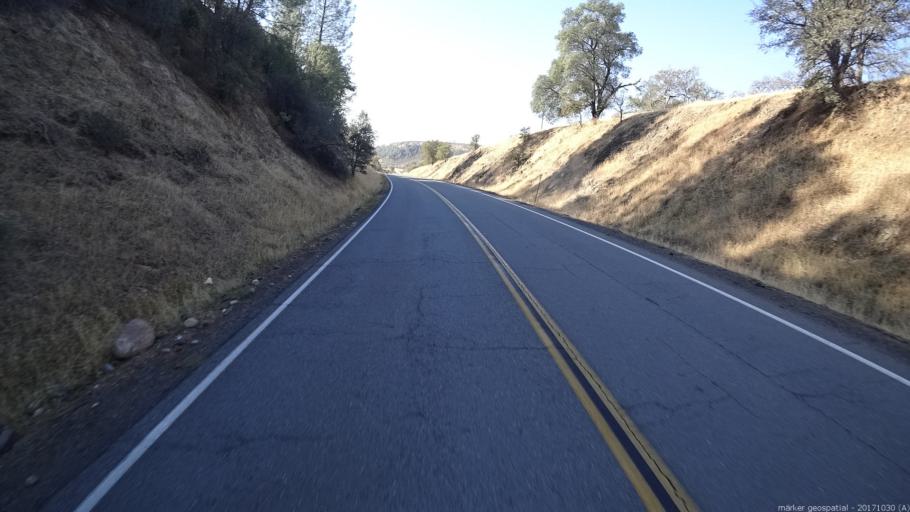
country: US
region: California
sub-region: Shasta County
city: Bella Vista
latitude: 40.6641
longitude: -122.0667
